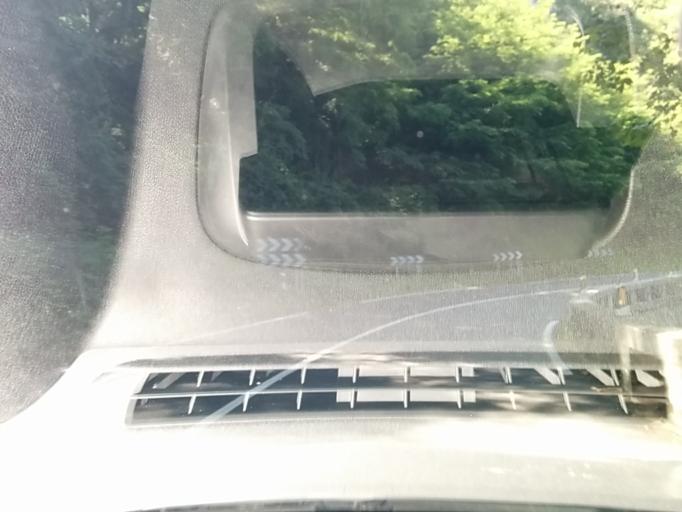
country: ES
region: Basque Country
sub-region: Provincia de Guipuzcoa
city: Mutriku
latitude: 43.3071
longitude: -2.3724
